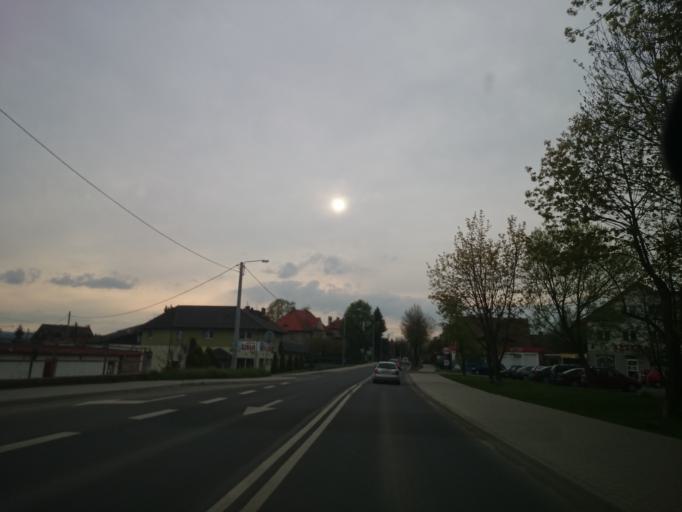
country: PL
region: Lower Silesian Voivodeship
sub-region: Powiat zabkowicki
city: Zabkowice Slaskie
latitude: 50.5878
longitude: 16.8241
